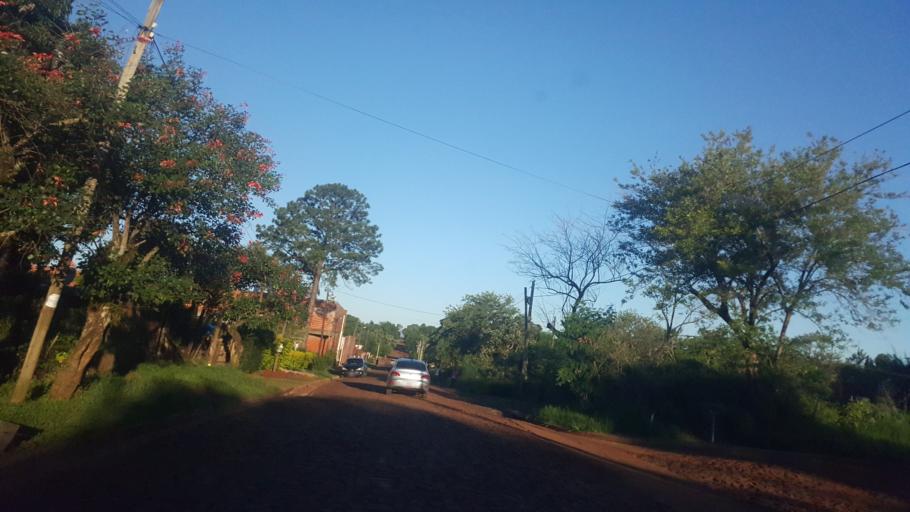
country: AR
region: Misiones
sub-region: Departamento de Capital
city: Posadas
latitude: -27.4227
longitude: -55.9262
